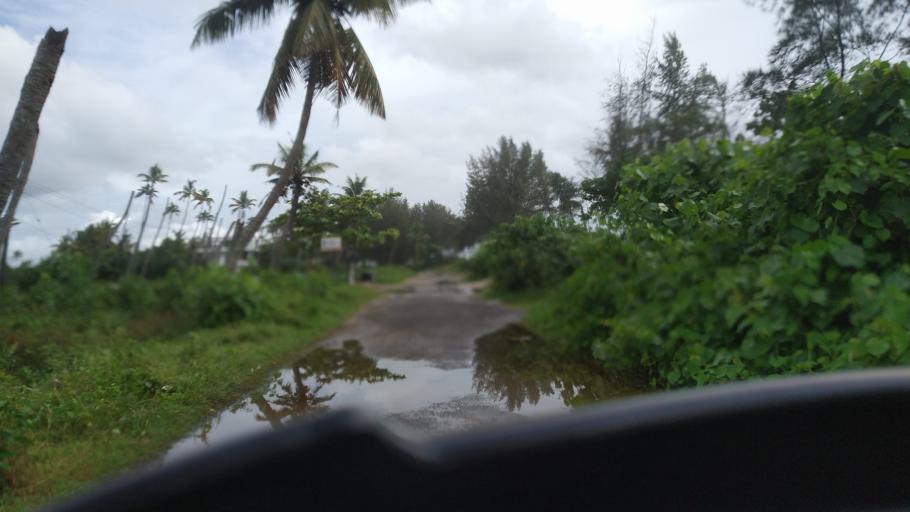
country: IN
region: Kerala
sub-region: Ernakulam
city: Elur
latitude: 10.1016
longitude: 76.1893
